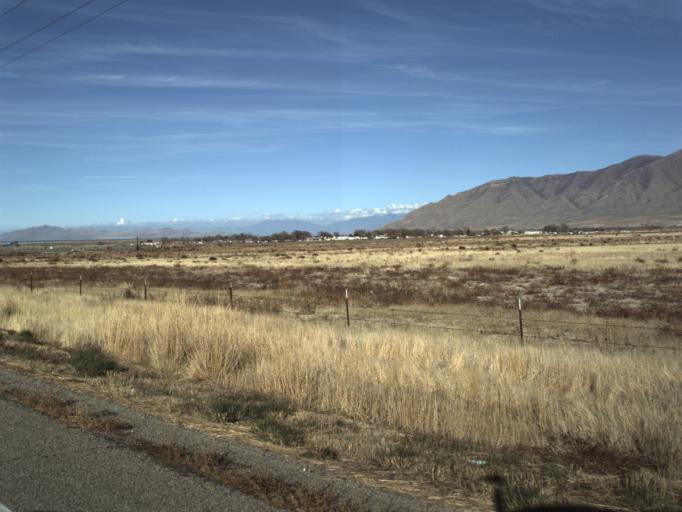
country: US
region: Utah
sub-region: Tooele County
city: Erda
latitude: 40.5905
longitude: -112.3703
